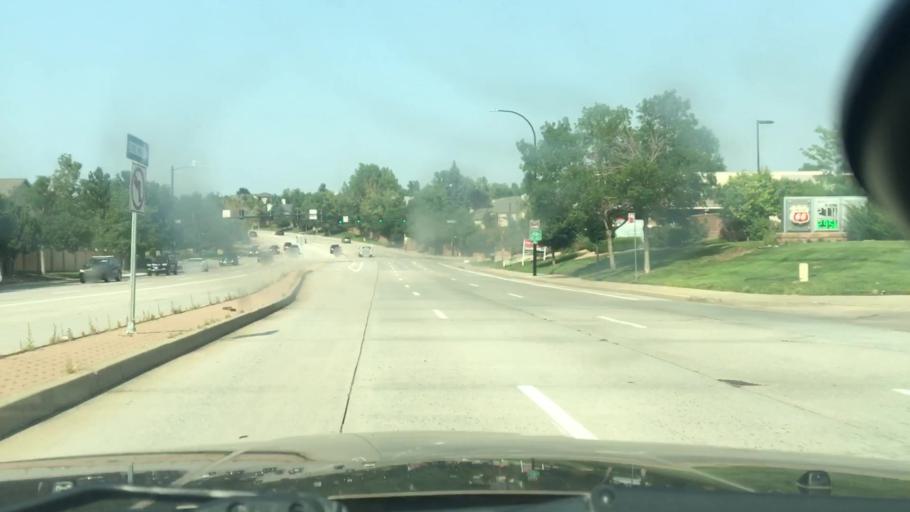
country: US
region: Colorado
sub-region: Douglas County
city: Carriage Club
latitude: 39.5426
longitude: -104.9126
